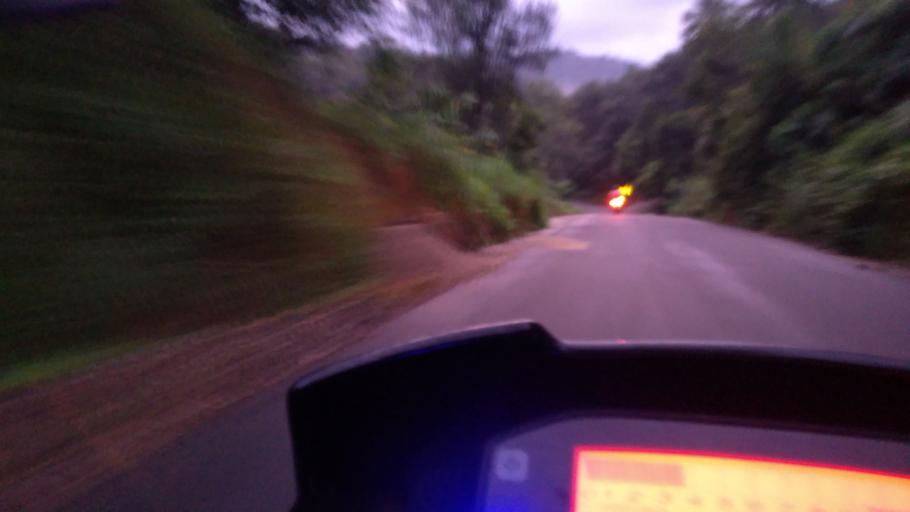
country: IN
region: Kerala
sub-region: Idukki
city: Munnar
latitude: 9.9643
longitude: 77.0682
